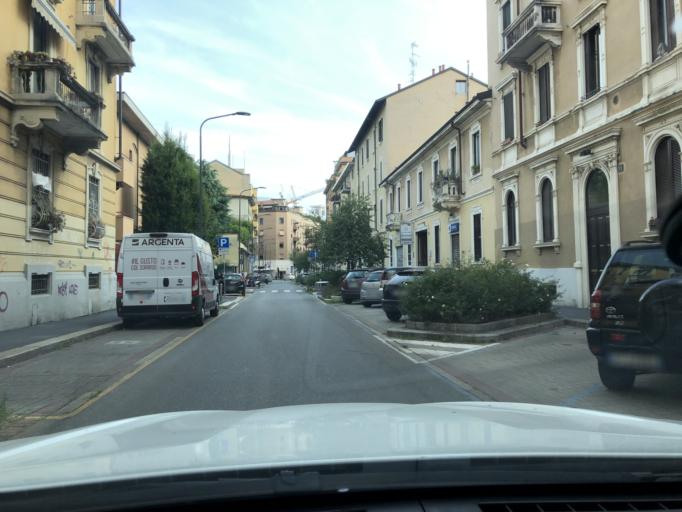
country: IT
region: Lombardy
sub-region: Citta metropolitana di Milano
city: Milano
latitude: 45.4917
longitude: 9.1878
